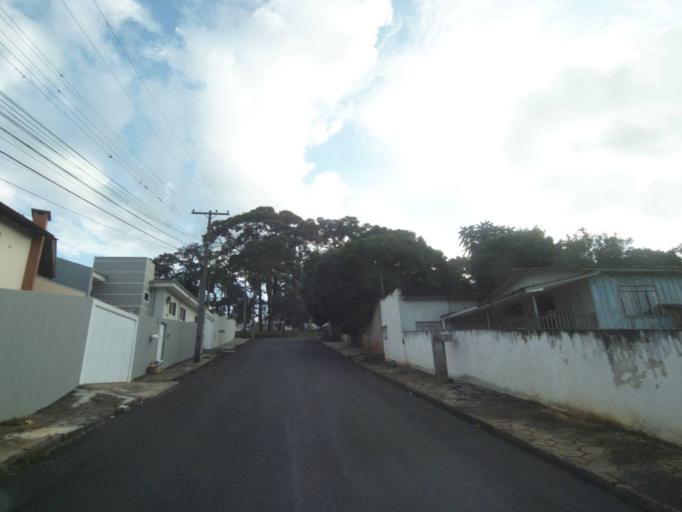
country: BR
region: Parana
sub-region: Telemaco Borba
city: Telemaco Borba
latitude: -24.3303
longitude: -50.6092
